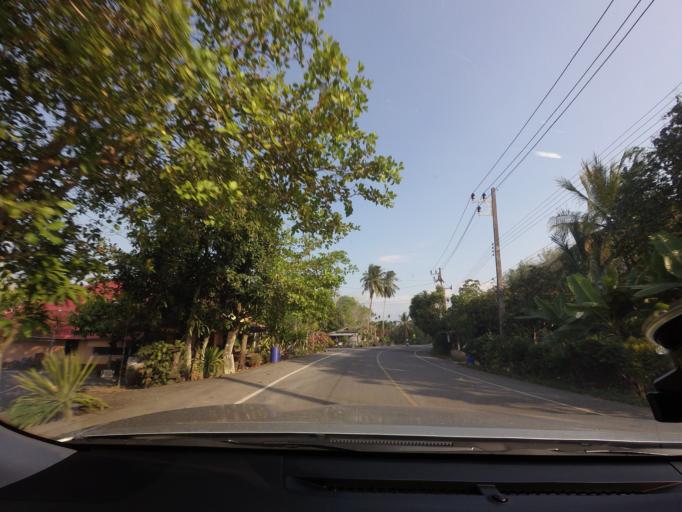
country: TH
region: Surat Thani
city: Phrasaeng
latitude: 8.5596
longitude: 99.2944
